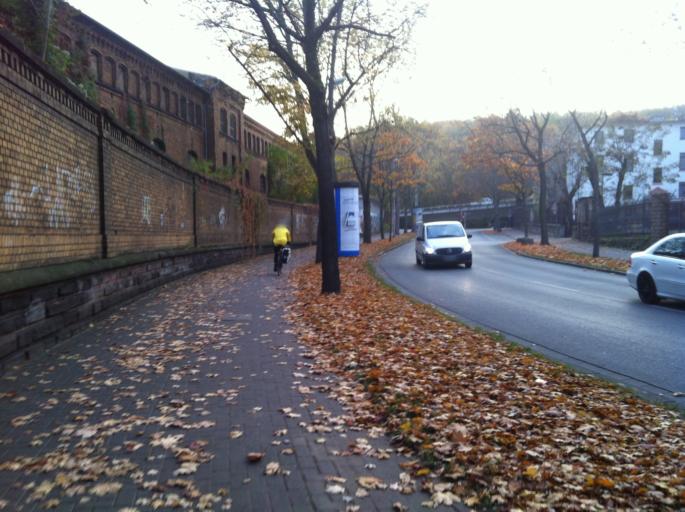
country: DE
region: Rheinland-Pfalz
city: Mainz
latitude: 50.0124
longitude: 8.2445
